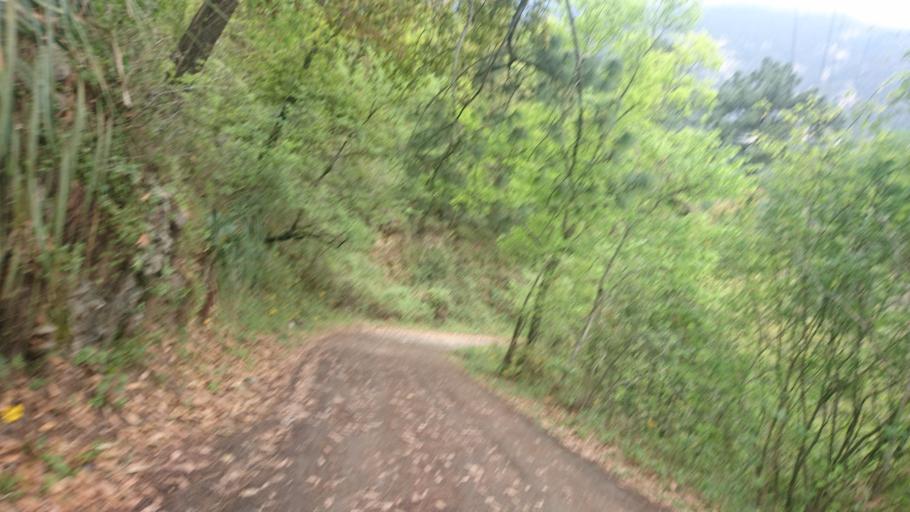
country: MX
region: Nuevo Leon
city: Garza Garcia
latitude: 25.6056
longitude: -100.3453
